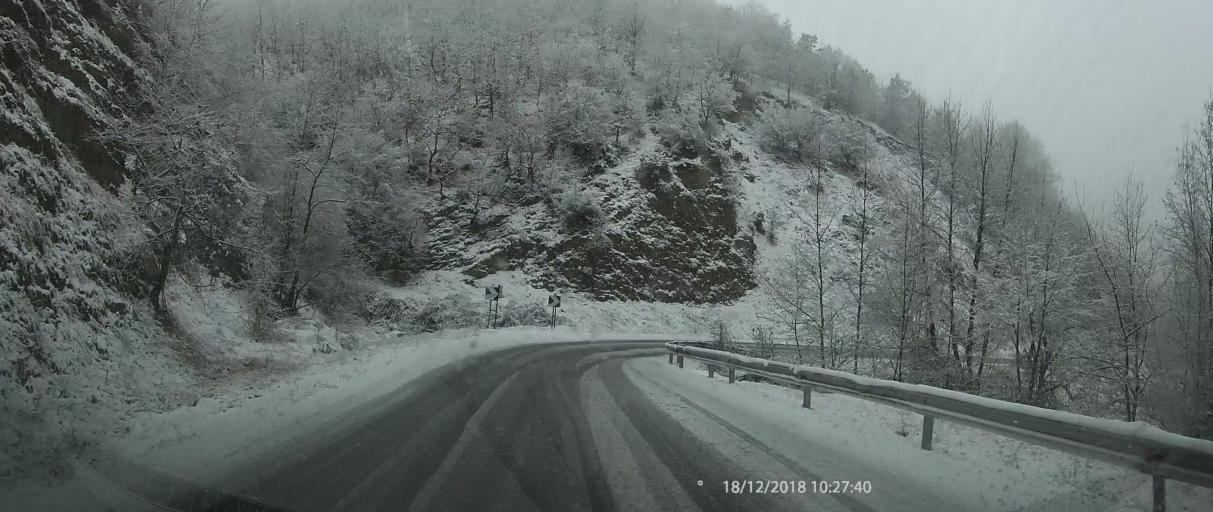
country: GR
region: Thessaly
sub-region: Nomos Larisis
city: Livadi
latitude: 40.1737
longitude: 22.2574
